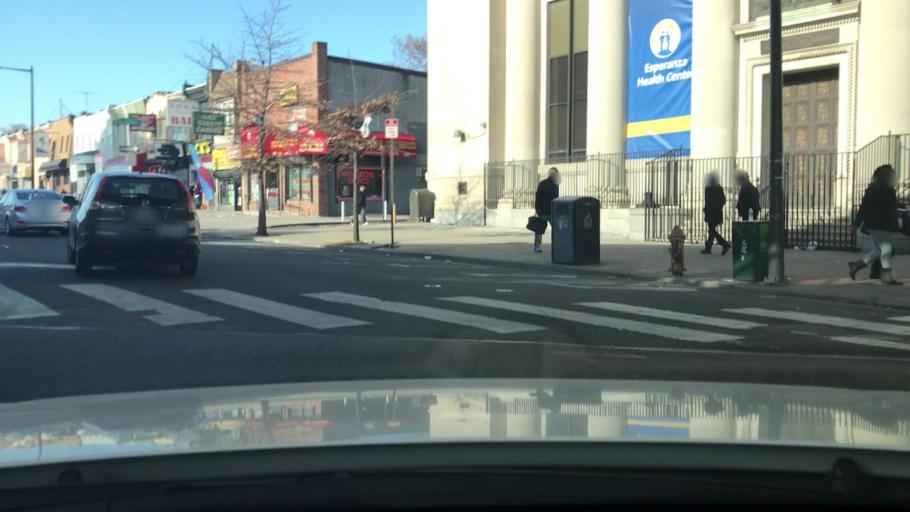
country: US
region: Pennsylvania
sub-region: Philadelphia County
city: Philadelphia
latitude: 39.9965
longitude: -75.1134
